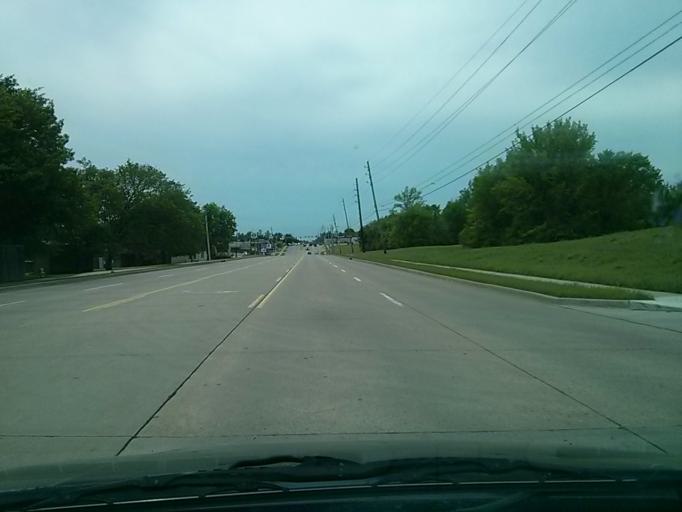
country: US
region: Oklahoma
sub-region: Tulsa County
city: Jenks
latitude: 36.0653
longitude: -95.9044
